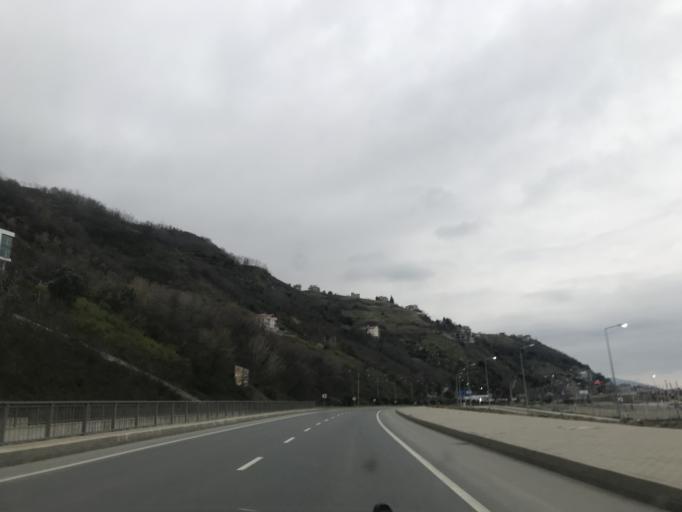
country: TR
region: Trabzon
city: Derecik
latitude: 40.9956
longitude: 39.6481
